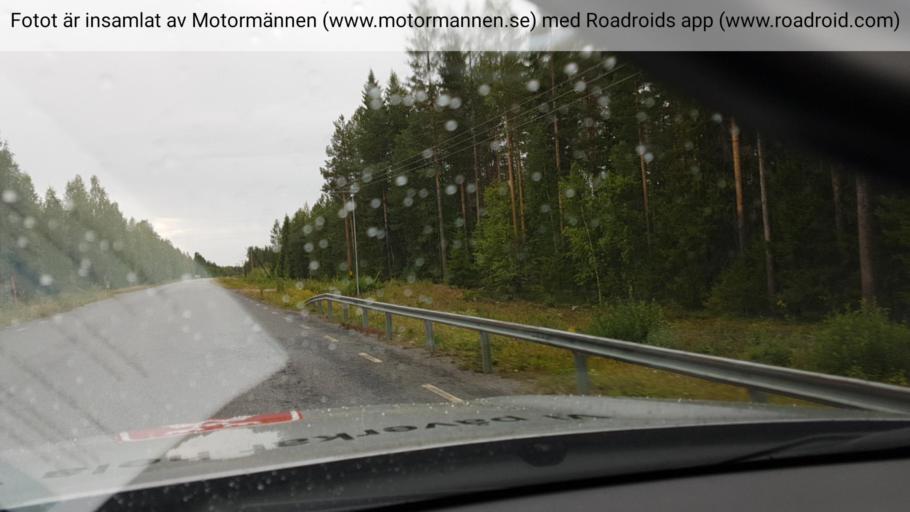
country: SE
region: Norrbotten
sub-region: Bodens Kommun
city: Boden
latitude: 65.8335
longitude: 21.4994
